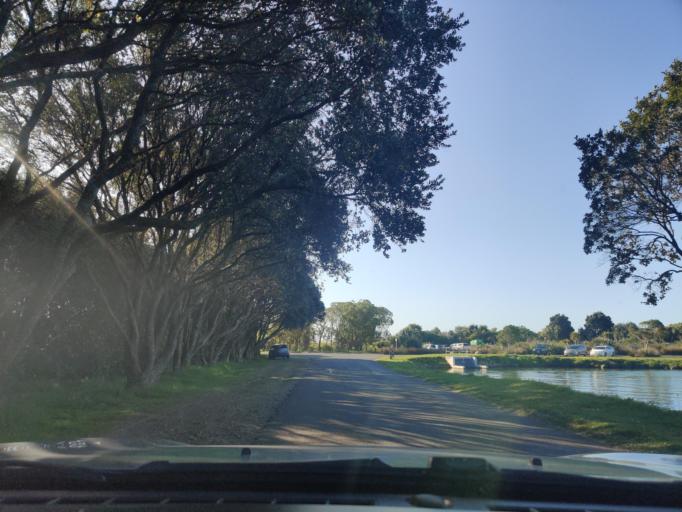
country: NZ
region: Taranaki
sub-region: New Plymouth District
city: New Plymouth
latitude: -39.0393
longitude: 174.1138
